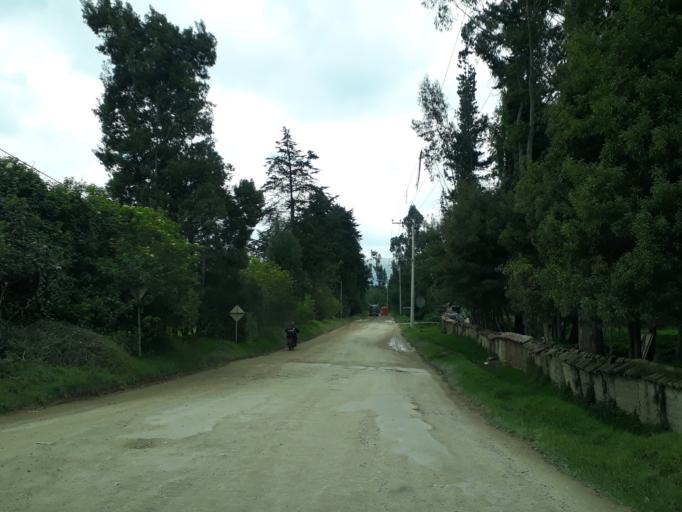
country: CO
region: Cundinamarca
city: Sesquile
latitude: 5.0622
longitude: -73.8036
